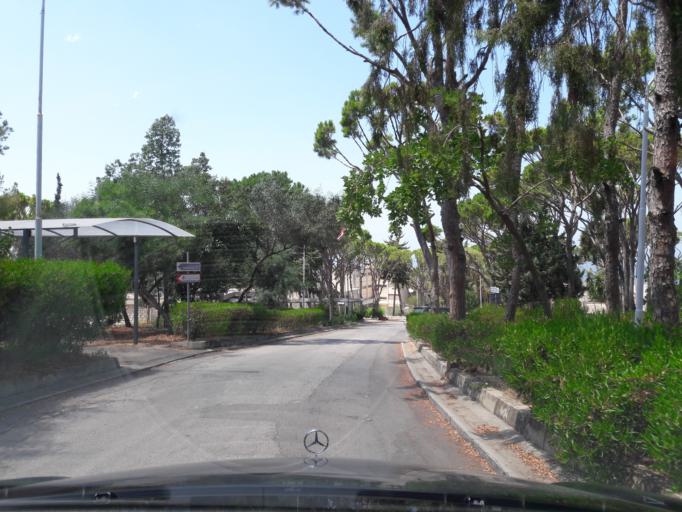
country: LB
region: Mont-Liban
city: Djounie
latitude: 33.9353
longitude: 35.6182
